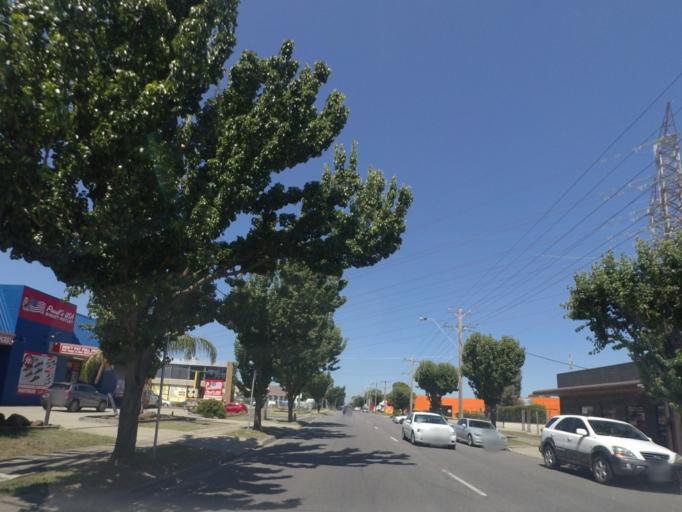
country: AU
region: Victoria
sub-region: Whittlesea
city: Thomastown
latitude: -37.6882
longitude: 145.0161
